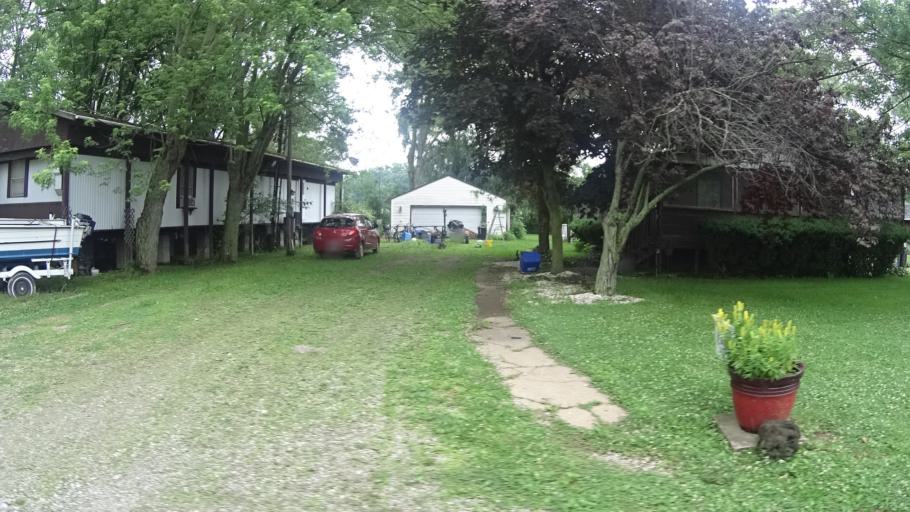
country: US
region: Ohio
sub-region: Erie County
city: Huron
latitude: 41.3520
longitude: -82.5575
